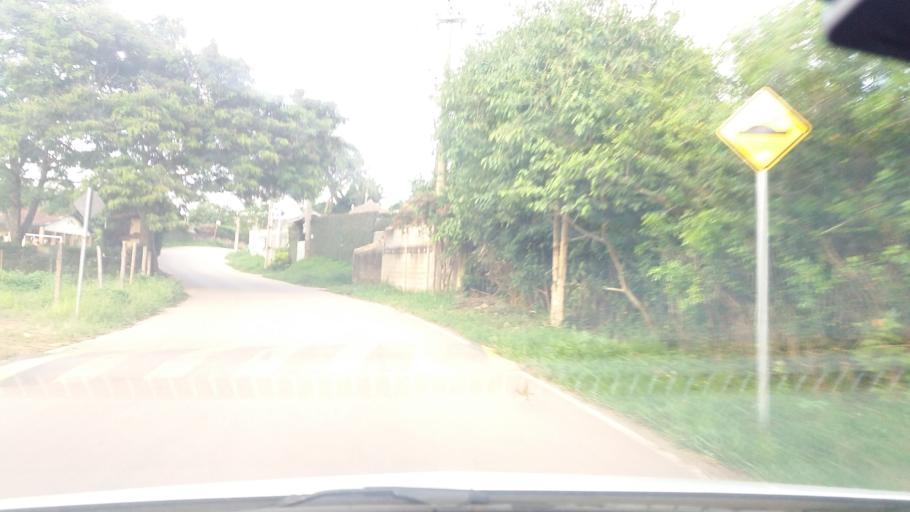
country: BR
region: Sao Paulo
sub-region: Bom Jesus Dos Perdoes
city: Bom Jesus dos Perdoes
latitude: -23.1767
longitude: -46.4837
